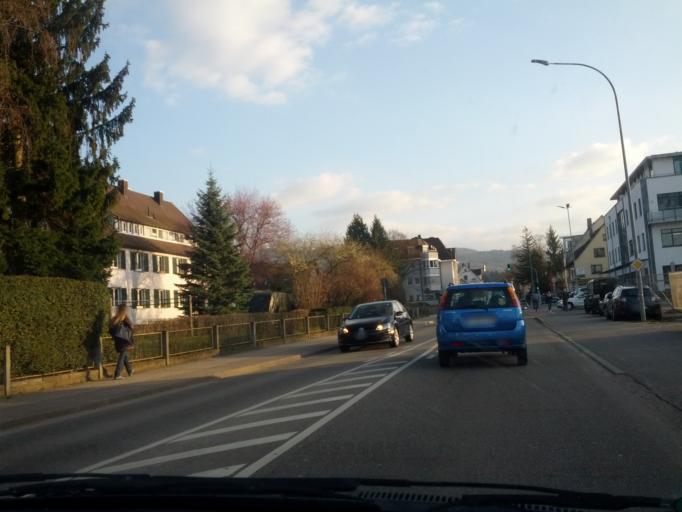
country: DE
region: Baden-Wuerttemberg
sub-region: Freiburg Region
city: Merzhausen
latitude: 47.9721
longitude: 7.8284
